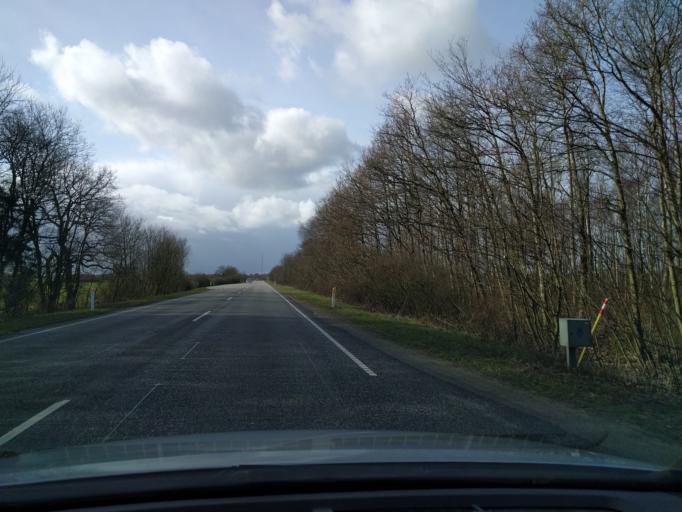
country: DK
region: South Denmark
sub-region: Kolding Kommune
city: Kolding
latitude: 55.4601
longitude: 9.3995
